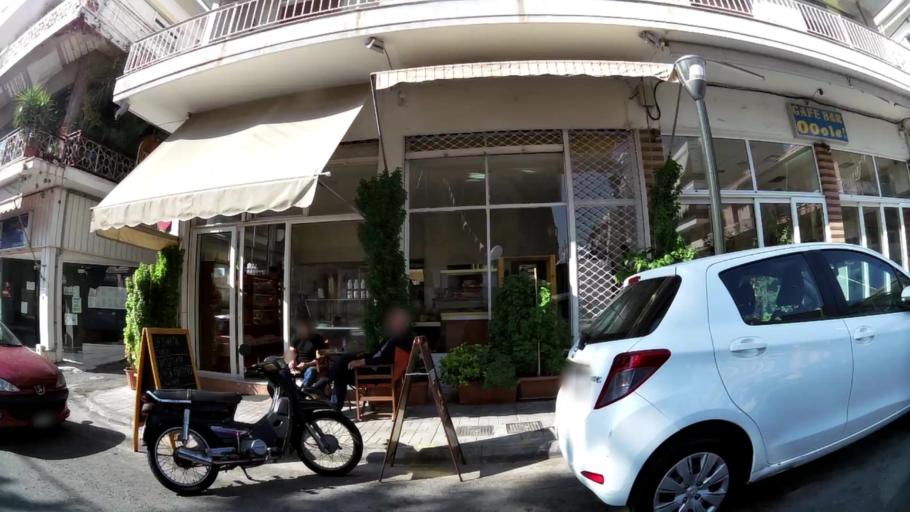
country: GR
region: Attica
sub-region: Nomos Piraios
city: Drapetsona
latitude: 37.9539
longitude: 23.6192
